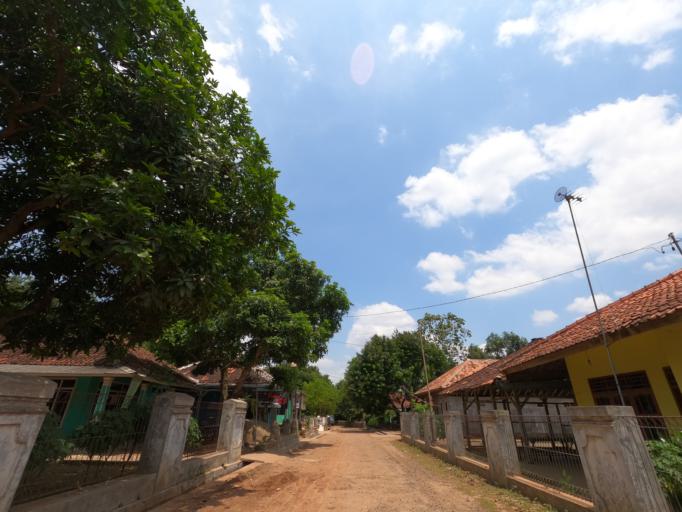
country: ID
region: West Java
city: Pamanukan
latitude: -6.5139
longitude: 107.7724
